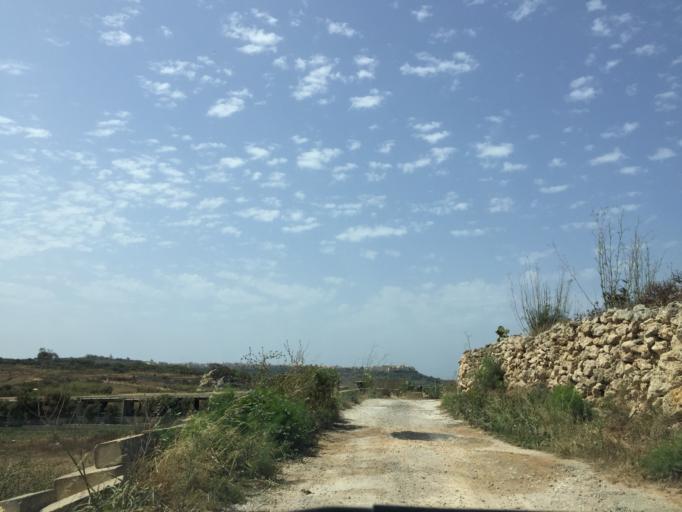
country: MT
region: In-Nadur
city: Nadur
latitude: 36.0596
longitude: 14.2904
